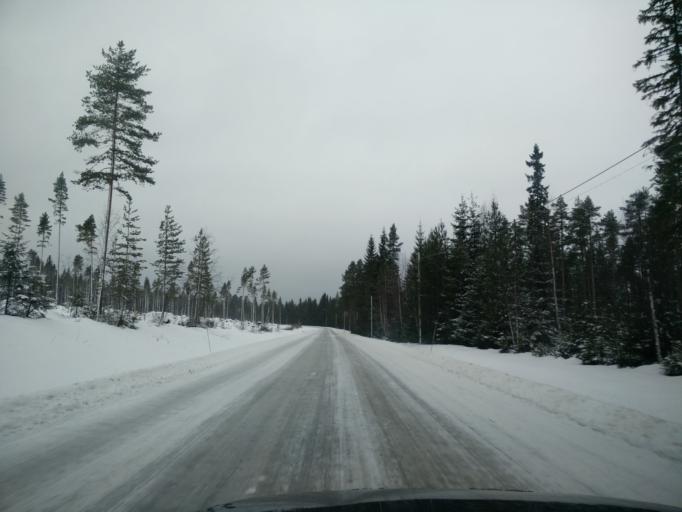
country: SE
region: Jaemtland
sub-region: Braecke Kommun
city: Braecke
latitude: 62.4034
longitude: 15.3116
